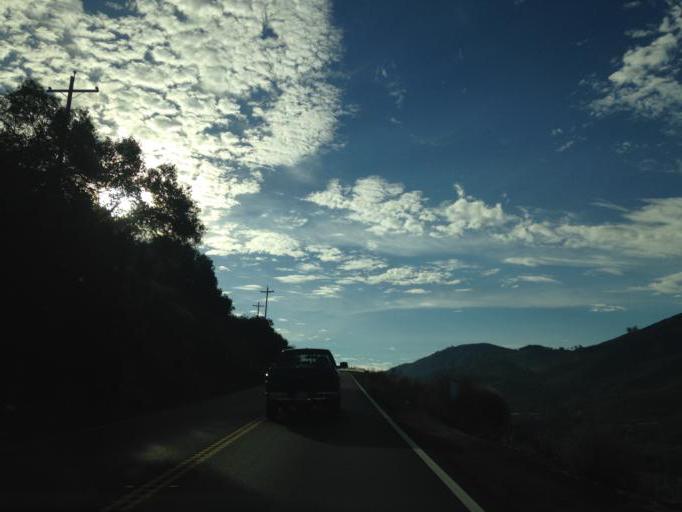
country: US
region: California
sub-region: San Diego County
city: Rainbow
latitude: 33.3578
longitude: -117.0392
